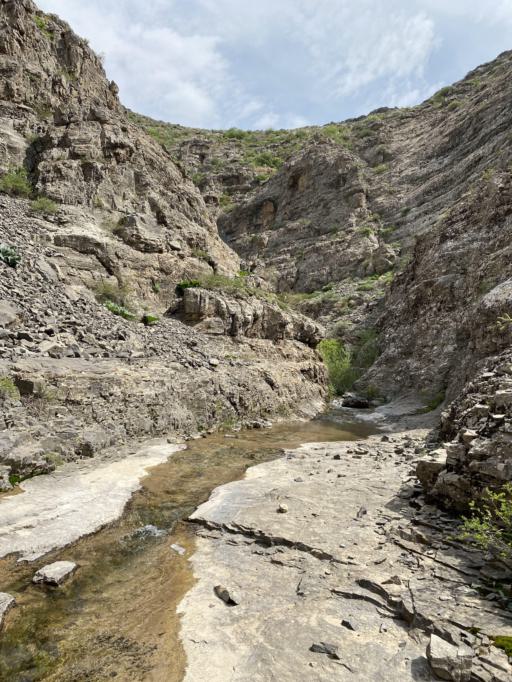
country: KZ
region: Ongtustik Qazaqstan
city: Ashchysay
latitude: 43.5325
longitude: 68.8446
